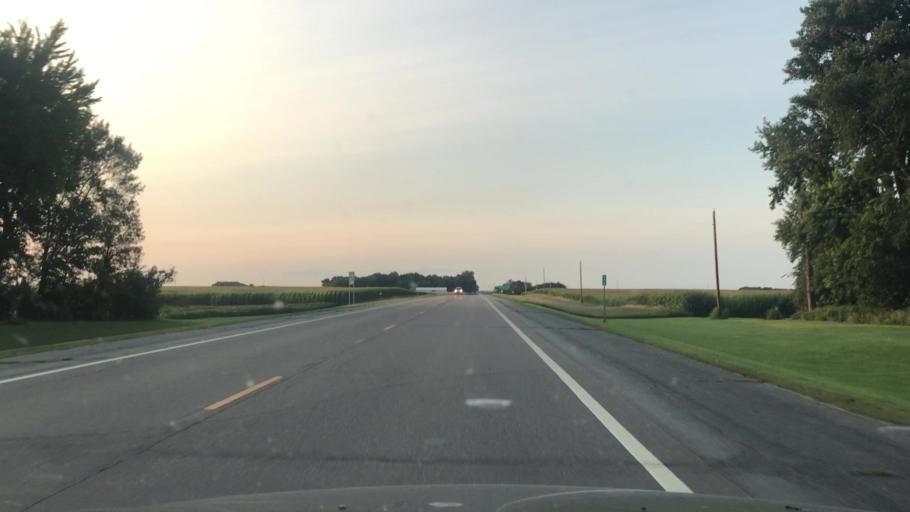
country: US
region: Minnesota
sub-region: Redwood County
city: Redwood Falls
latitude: 44.4079
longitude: -95.1276
